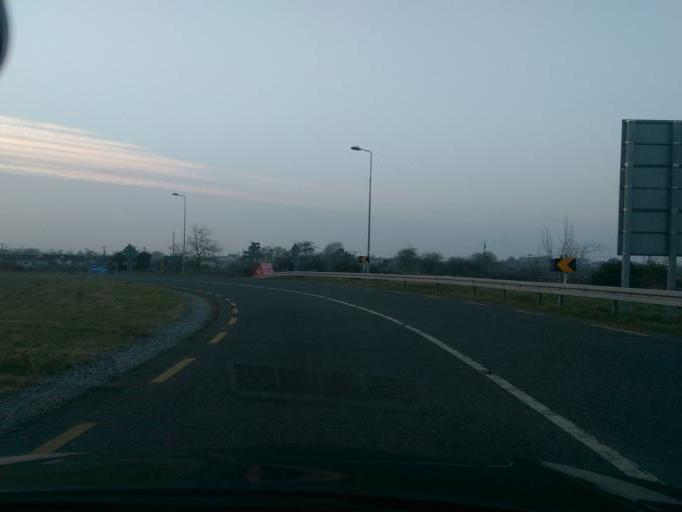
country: IE
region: Connaught
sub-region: County Galway
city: Loughrea
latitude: 53.2056
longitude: -8.5958
